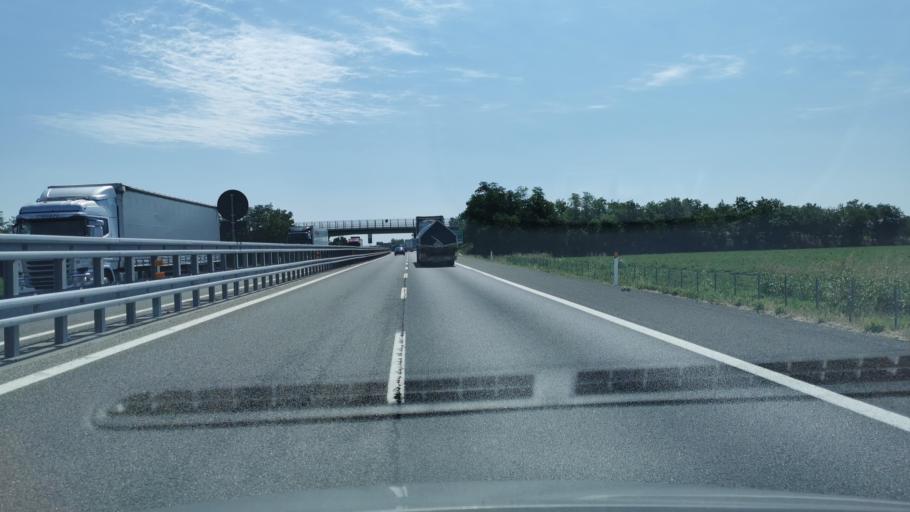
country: IT
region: Emilia-Romagna
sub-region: Provincia di Piacenza
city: Castel San Giovanni
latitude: 45.0775
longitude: 9.4379
